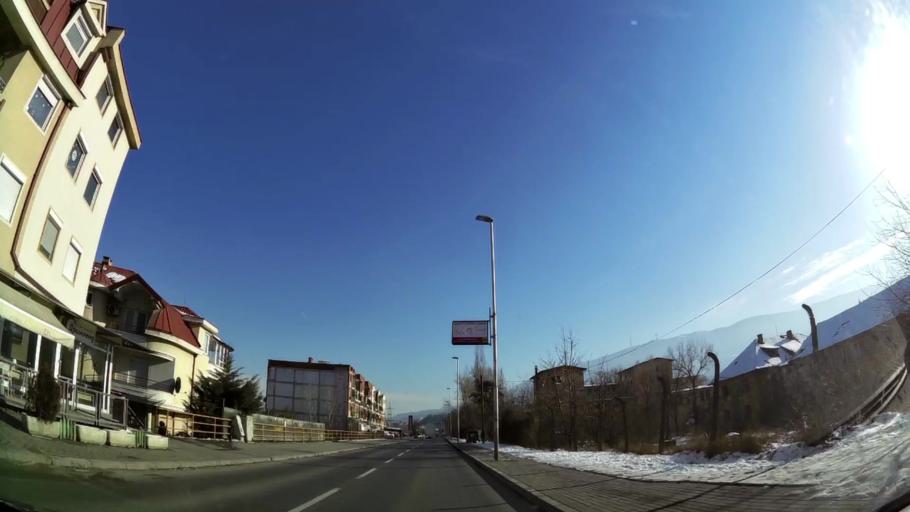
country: MK
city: Krushopek
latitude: 42.0027
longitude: 21.3752
